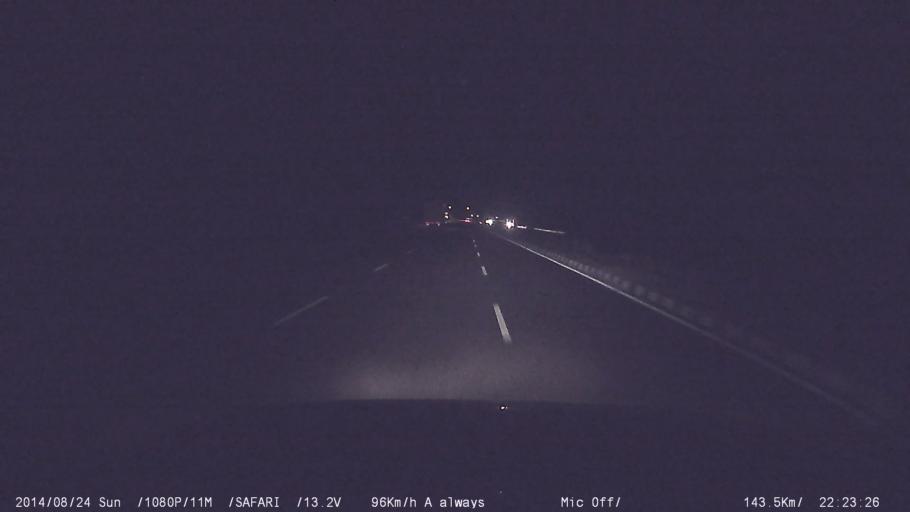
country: IN
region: Tamil Nadu
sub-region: Vellore
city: Jolarpettai
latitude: 12.6112
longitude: 78.5544
